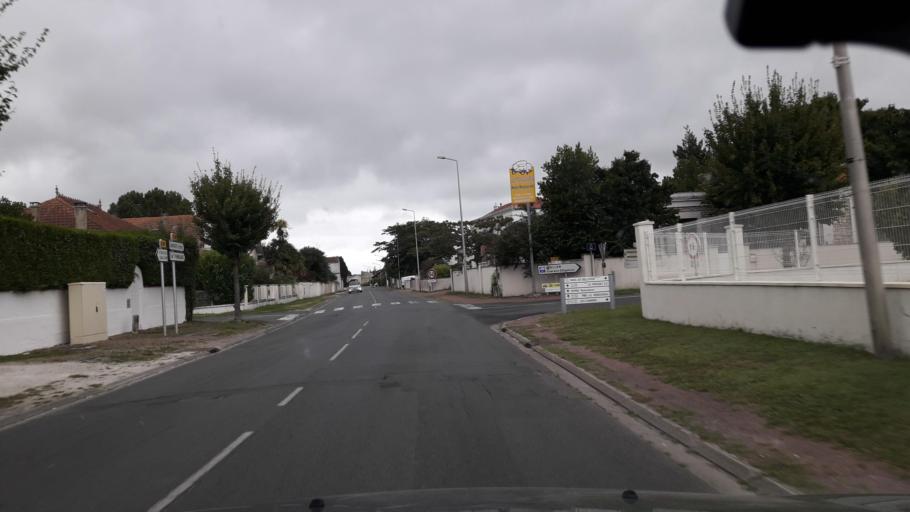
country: FR
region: Poitou-Charentes
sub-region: Departement de la Charente-Maritime
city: Arvert
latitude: 45.7396
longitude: -1.1130
